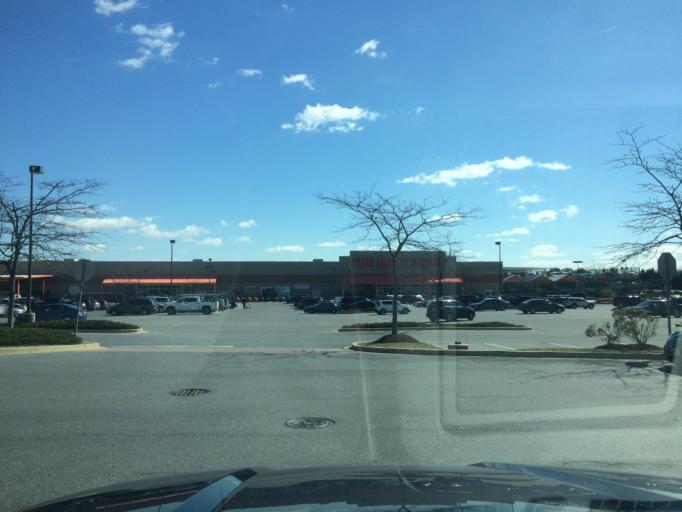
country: US
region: Maryland
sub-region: Carroll County
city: Eldersburg
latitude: 39.4093
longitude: -76.9486
